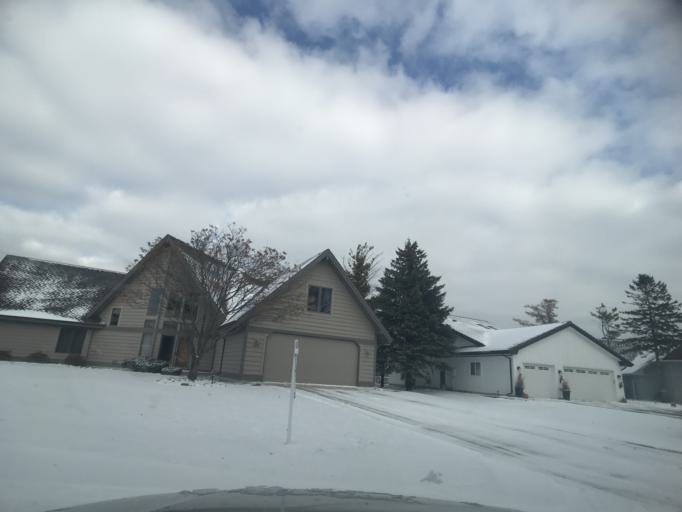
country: US
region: Wisconsin
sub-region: Door County
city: Sturgeon Bay
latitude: 44.8227
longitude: -87.3697
